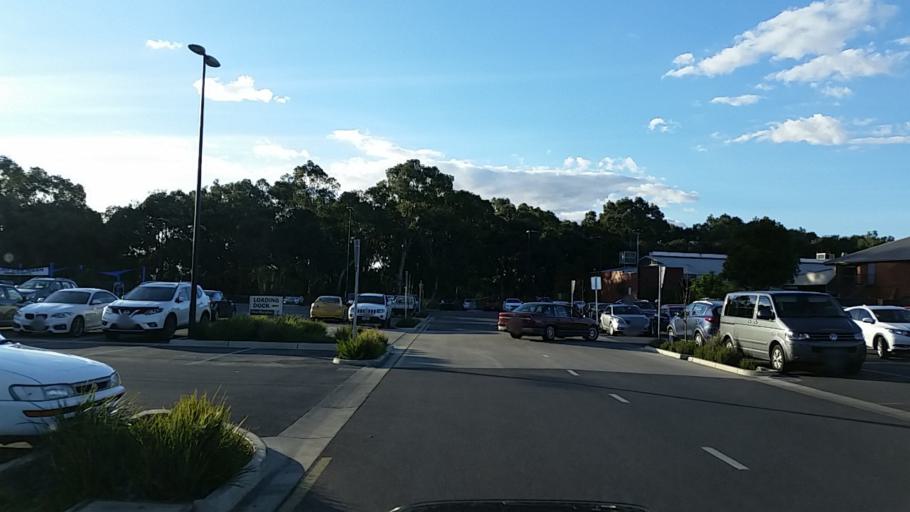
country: AU
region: South Australia
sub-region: City of West Torrens
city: Thebarton
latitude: -34.9137
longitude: 138.5628
